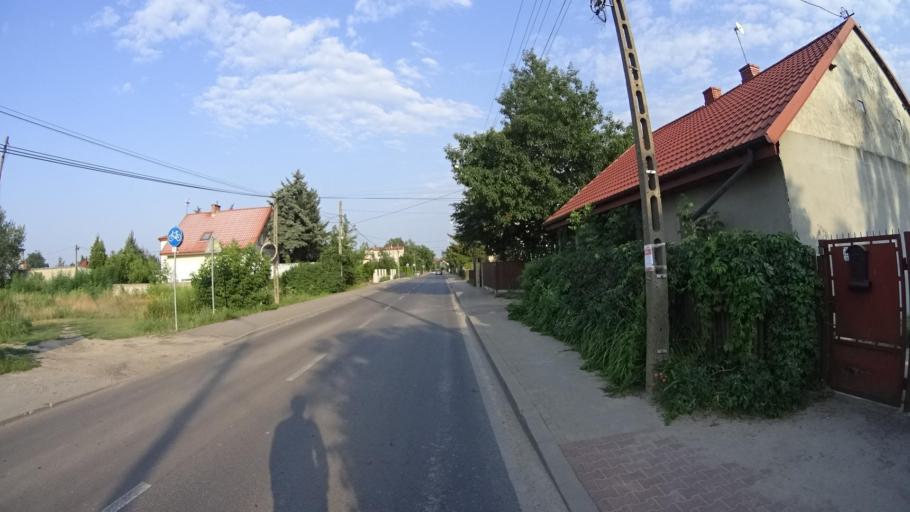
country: PL
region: Masovian Voivodeship
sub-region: Powiat pruszkowski
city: Rybie
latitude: 52.1466
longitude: 20.9463
